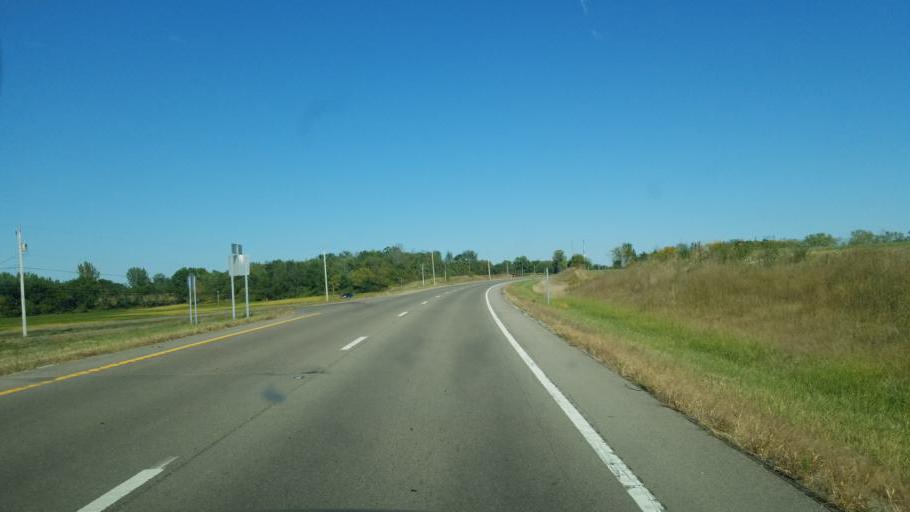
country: US
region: Ohio
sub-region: Clark County
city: Lisbon
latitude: 39.9254
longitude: -83.6554
